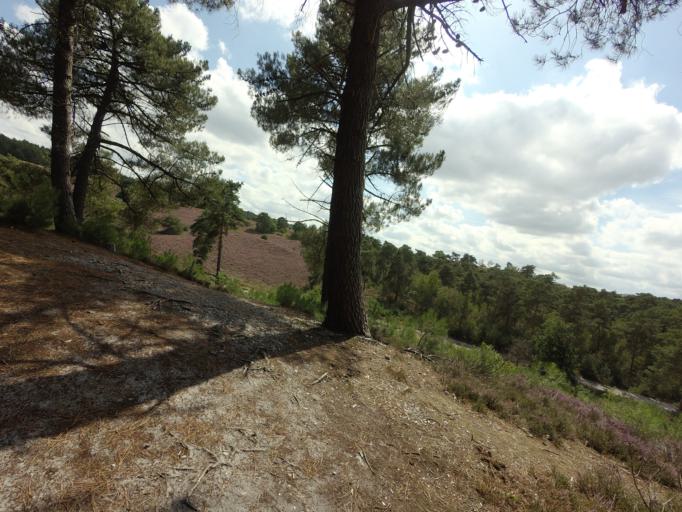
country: NL
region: Limburg
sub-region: Gemeente Brunssum
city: Brunssum
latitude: 50.9241
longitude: 6.0054
